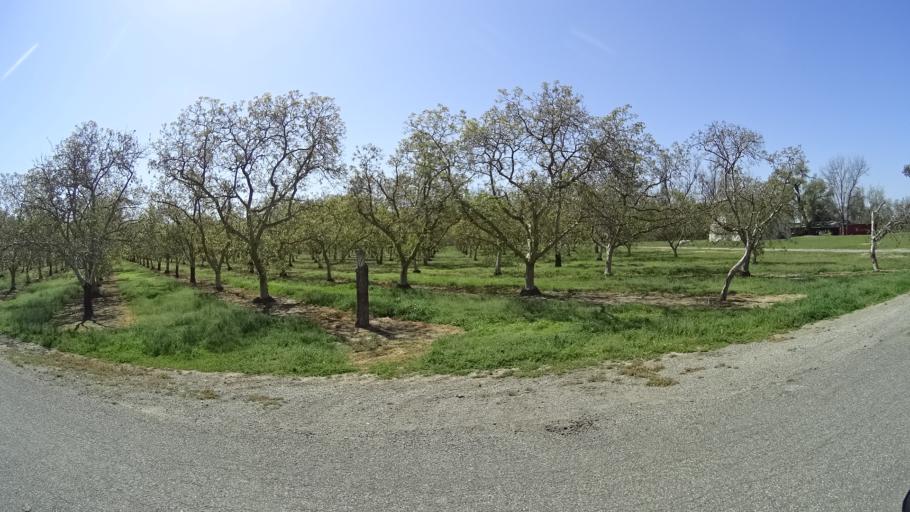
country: US
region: California
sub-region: Glenn County
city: Willows
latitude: 39.4355
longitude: -122.0163
